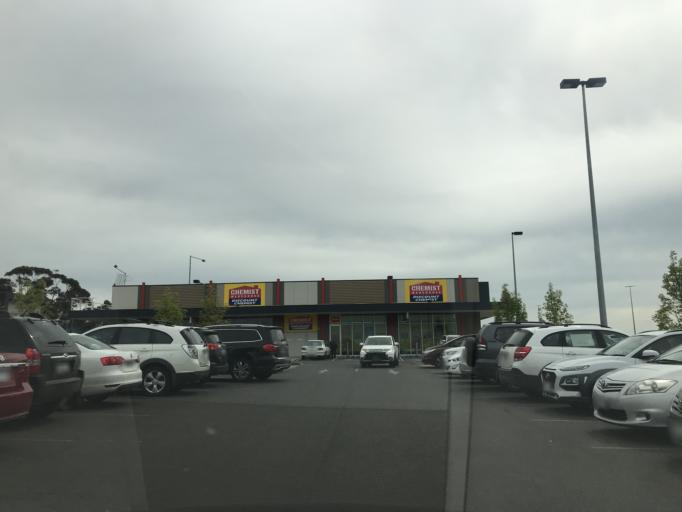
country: AU
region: Victoria
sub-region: Wyndham
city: Tarneit
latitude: -37.8402
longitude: 144.6747
